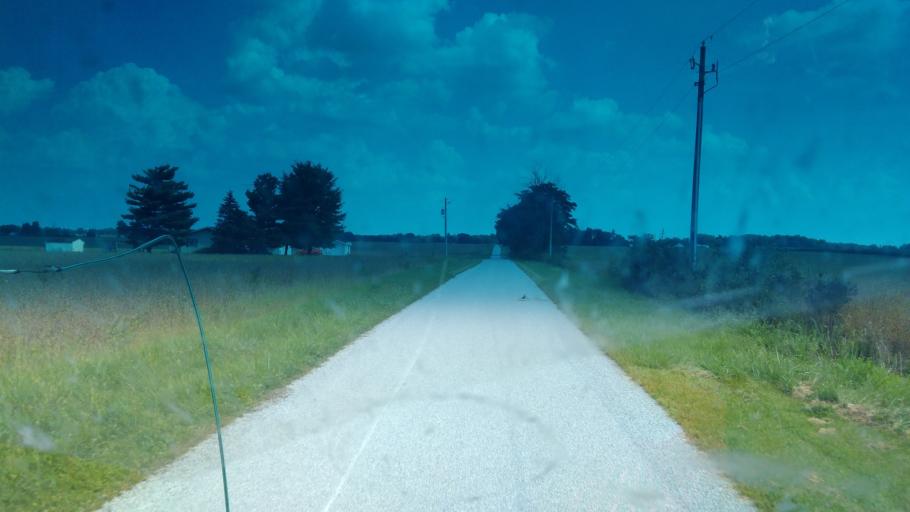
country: US
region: Ohio
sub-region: Hardin County
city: Ada
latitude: 40.7148
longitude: -83.7815
